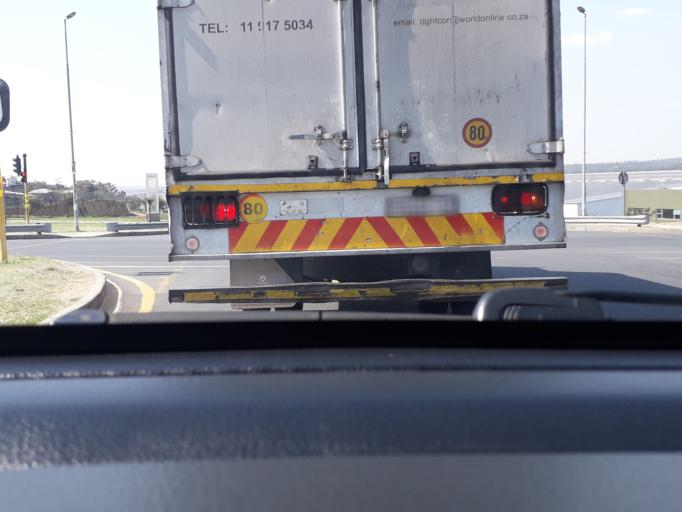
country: ZA
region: Gauteng
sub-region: City of Johannesburg Metropolitan Municipality
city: Modderfontein
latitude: -26.1045
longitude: 28.1382
